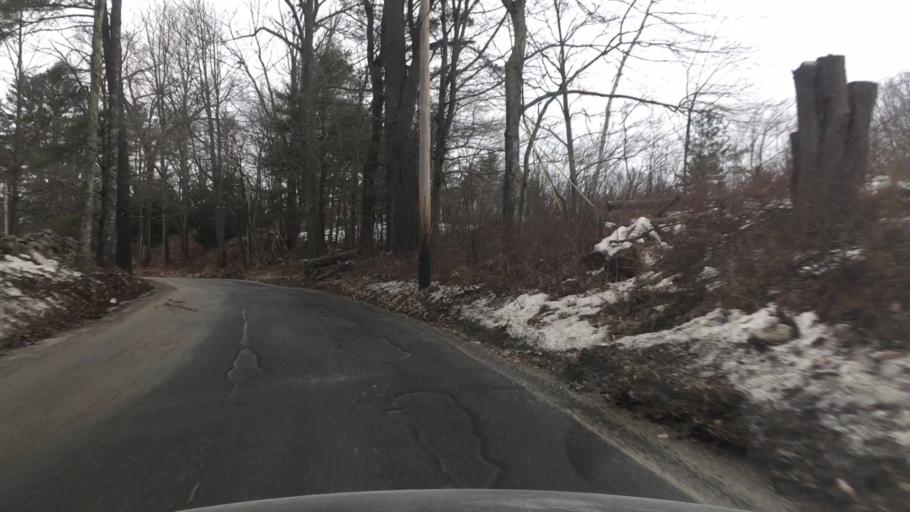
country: US
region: New Hampshire
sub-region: Hillsborough County
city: New Boston
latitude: 43.0070
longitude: -71.6671
